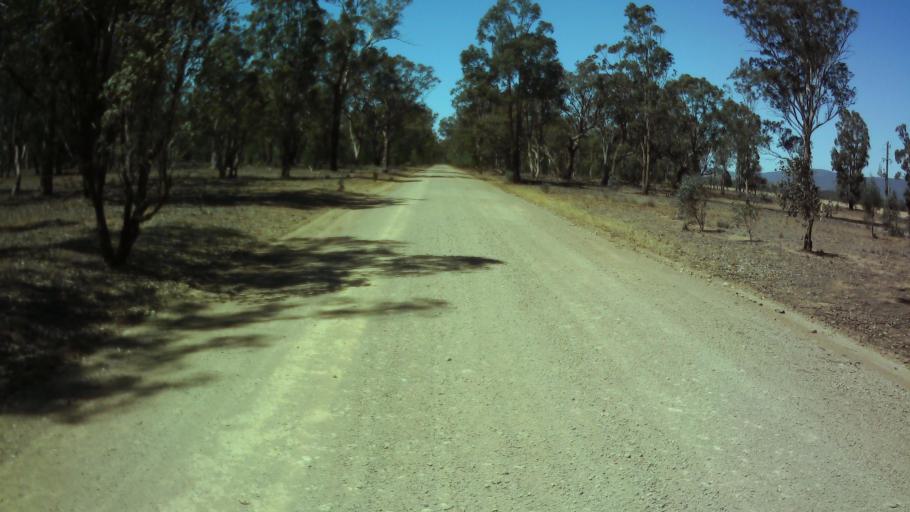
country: AU
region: New South Wales
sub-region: Weddin
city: Grenfell
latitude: -33.8529
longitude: 148.0879
